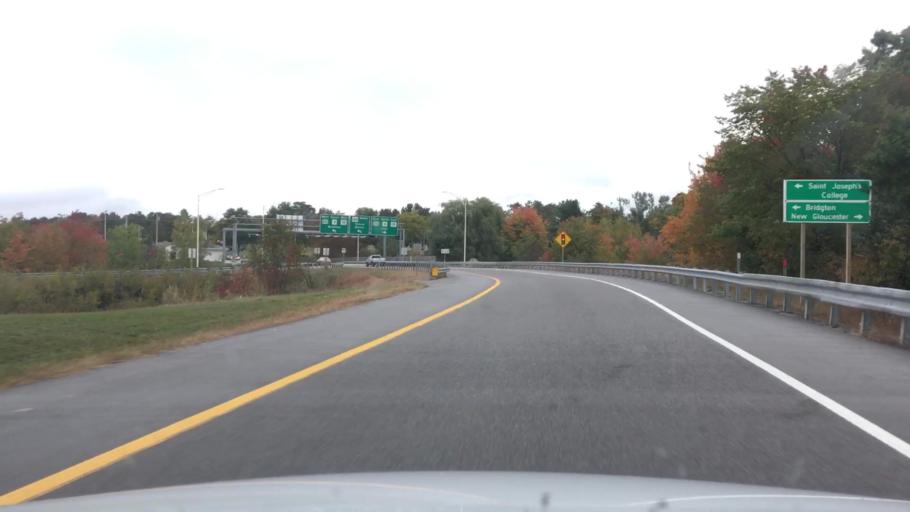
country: US
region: Maine
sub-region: Cumberland County
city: New Gloucester
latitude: 43.8814
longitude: -70.3333
